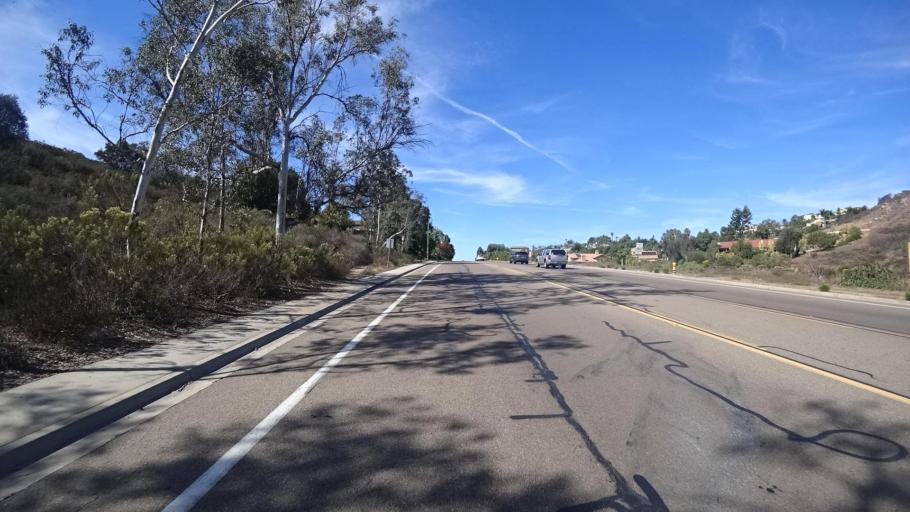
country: US
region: California
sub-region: San Diego County
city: Rancho San Diego
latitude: 32.7513
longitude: -116.9468
